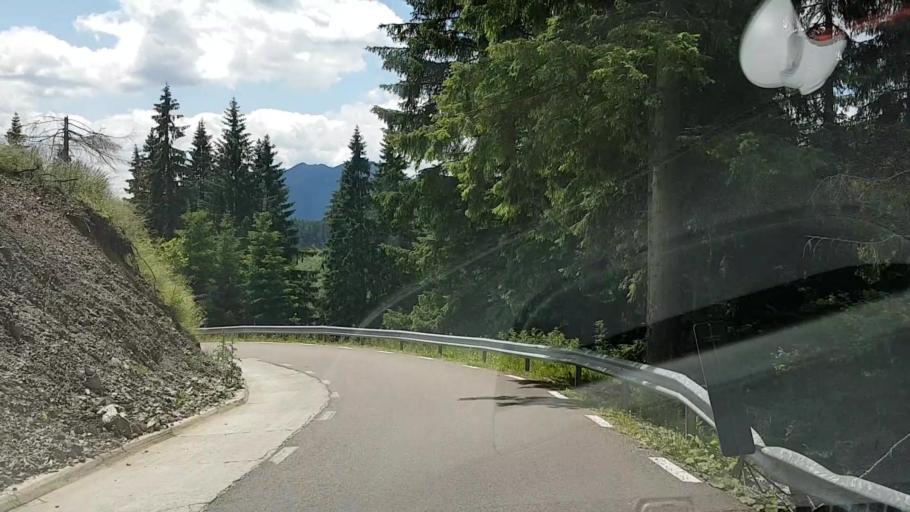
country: RO
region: Suceava
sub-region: Municipiul Campulung Moldovenesc
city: Campulung Moldovenesc
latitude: 47.4382
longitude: 25.5589
